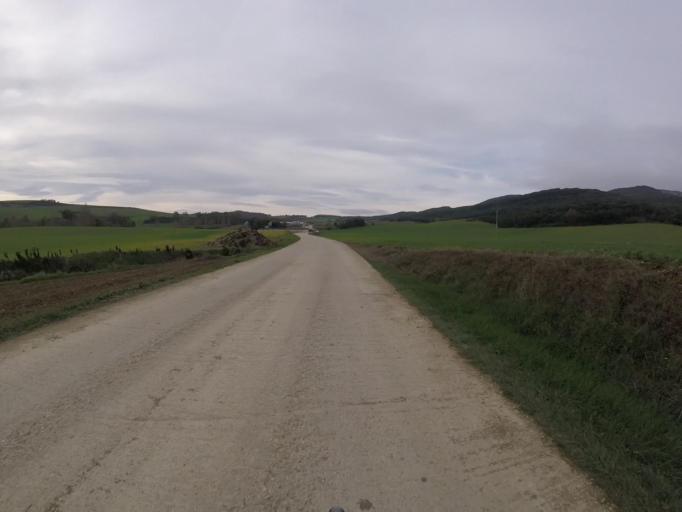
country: ES
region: Navarre
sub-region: Provincia de Navarra
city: Estella
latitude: 42.7253
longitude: -2.0277
